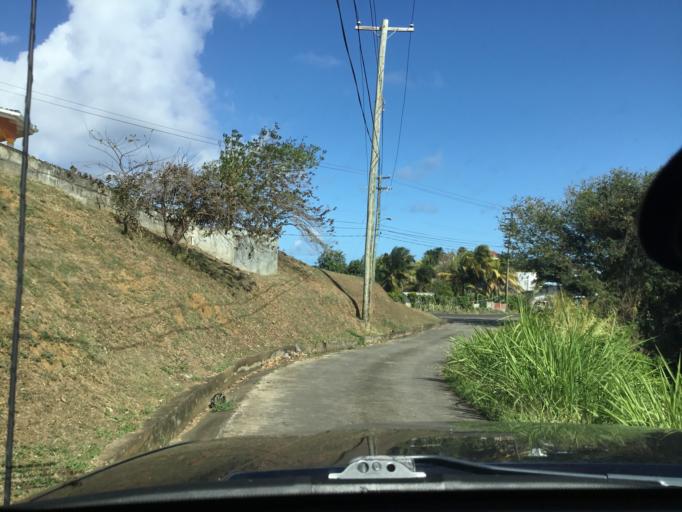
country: VC
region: Charlotte
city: Biabou
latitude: 13.1601
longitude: -61.1599
